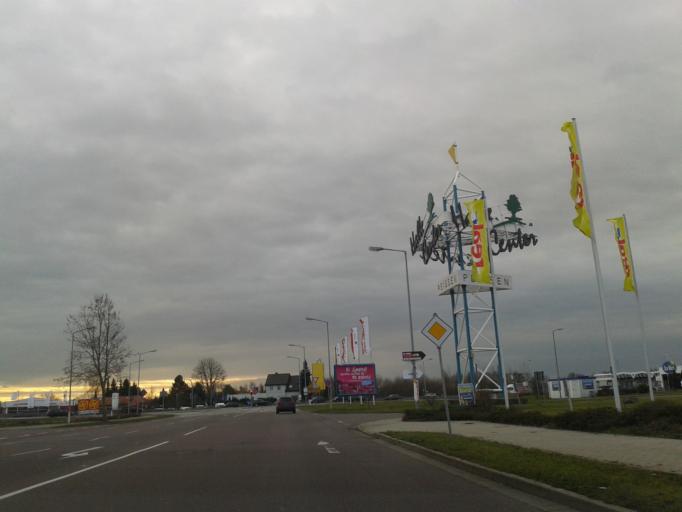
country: DE
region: Saxony-Anhalt
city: Peissen
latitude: 51.5107
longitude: 12.0541
